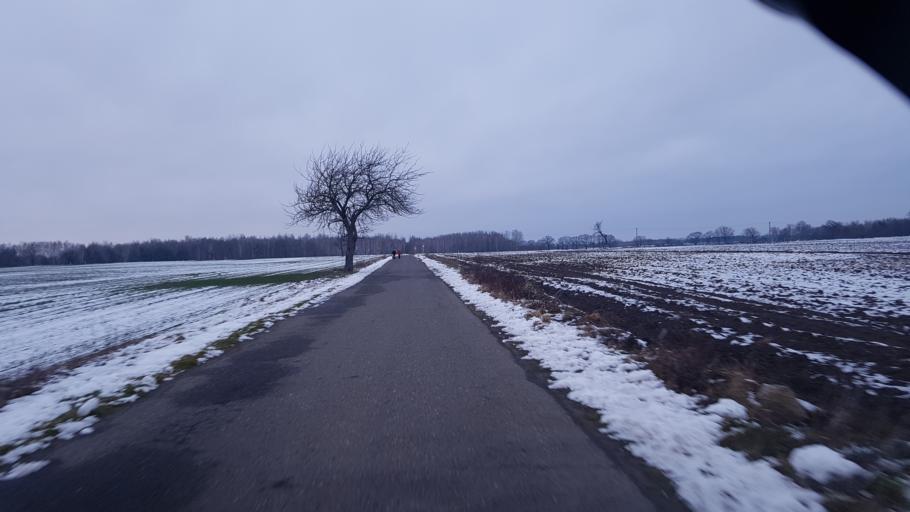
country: DE
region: Brandenburg
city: Vetschau
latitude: 51.7857
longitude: 14.0276
